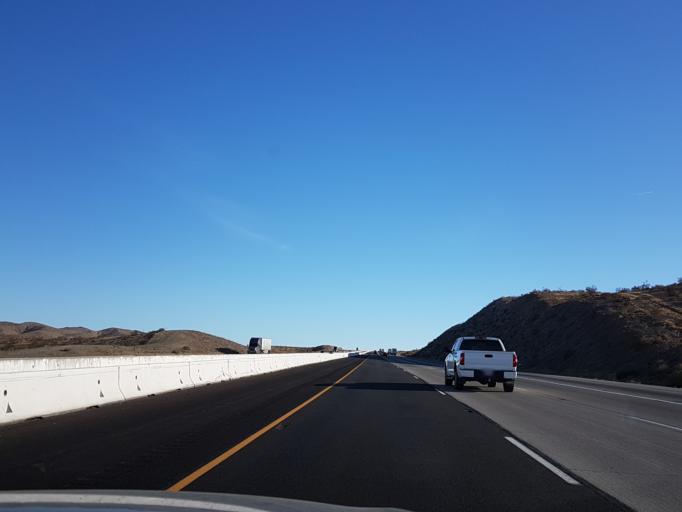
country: US
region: California
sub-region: San Bernardino County
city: Victorville
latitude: 34.6812
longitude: -117.2130
